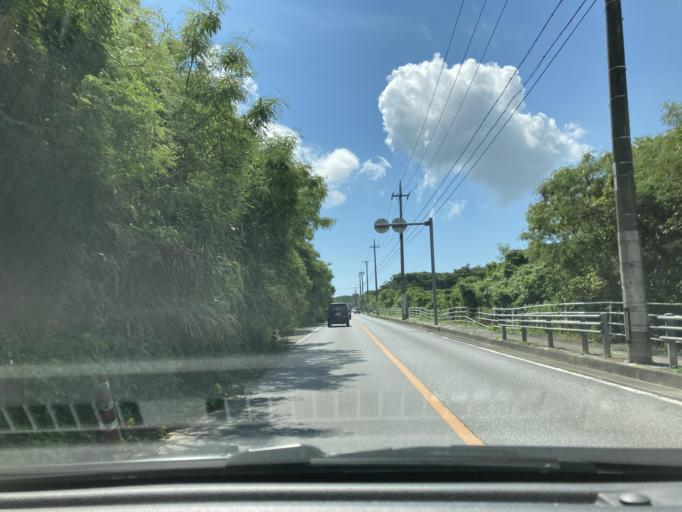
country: JP
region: Okinawa
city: Tomigusuku
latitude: 26.1596
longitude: 127.7712
